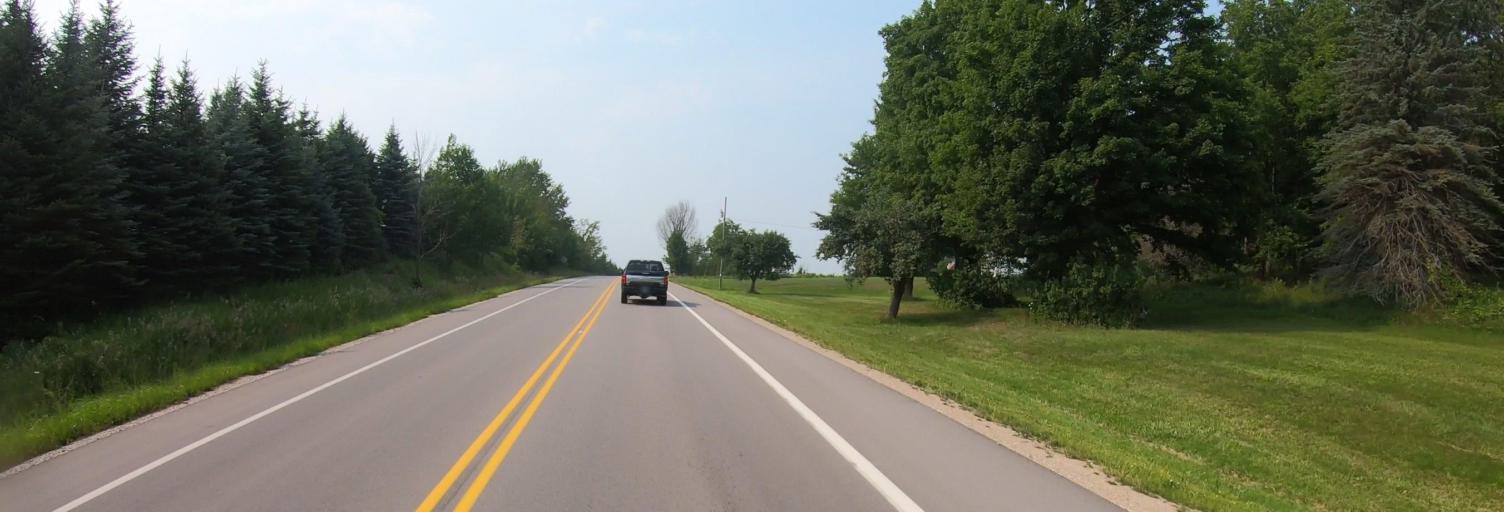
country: US
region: Michigan
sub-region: Charlevoix County
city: Charlevoix
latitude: 45.2566
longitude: -85.2621
